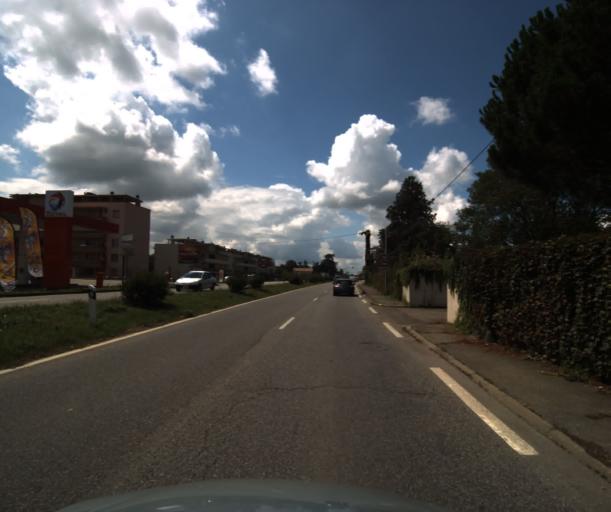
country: FR
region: Midi-Pyrenees
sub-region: Departement de la Haute-Garonne
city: Portet-sur-Garonne
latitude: 43.5253
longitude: 1.4007
